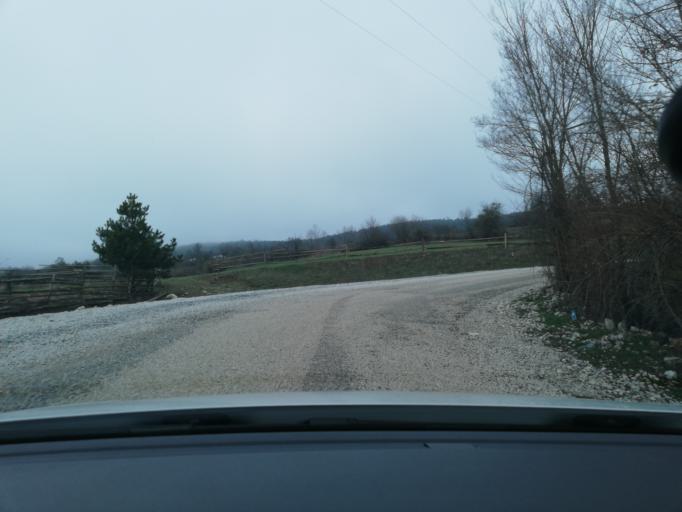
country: TR
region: Bolu
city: Bolu
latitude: 40.6609
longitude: 31.4636
